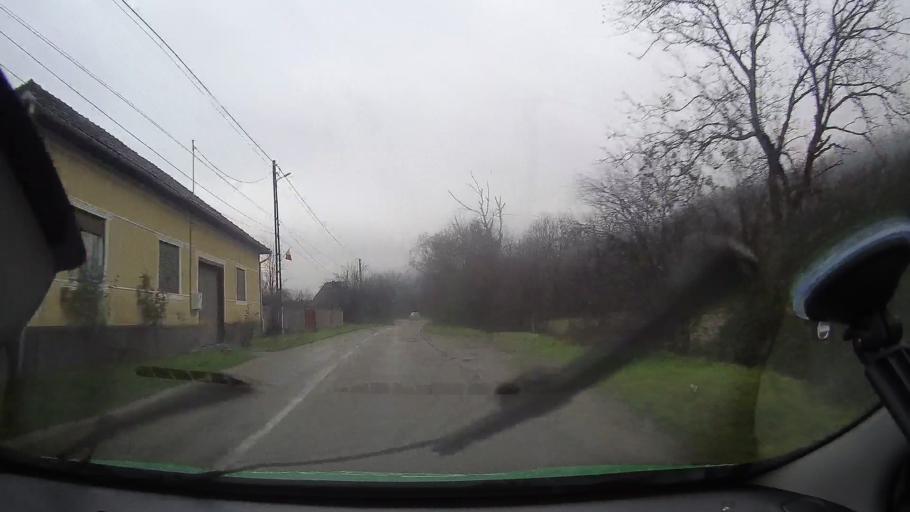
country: RO
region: Arad
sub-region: Comuna Moneasa
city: Moneasa
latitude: 46.4308
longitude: 22.2528
